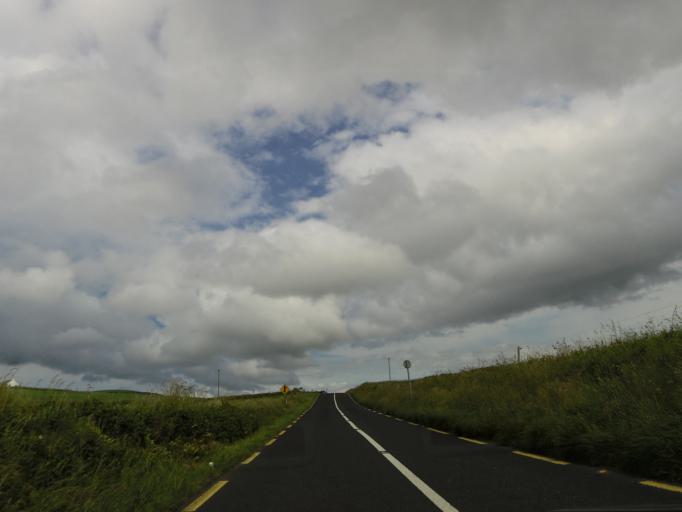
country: IE
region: Munster
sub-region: An Clar
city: Kilrush
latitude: 52.6962
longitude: -9.6303
